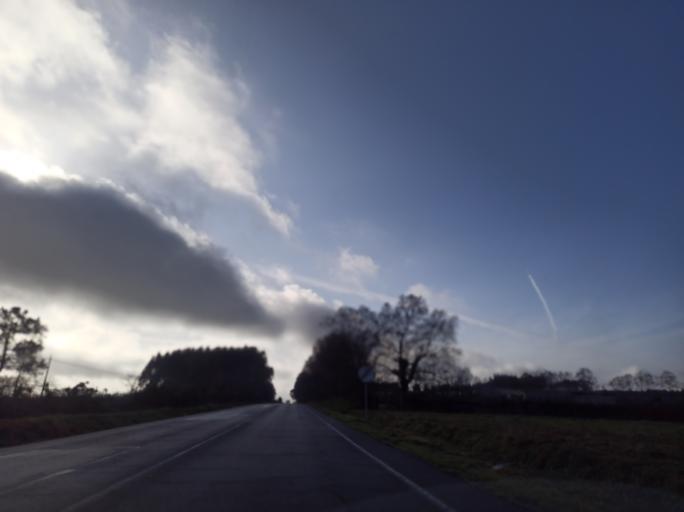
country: ES
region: Galicia
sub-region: Provincia da Coruna
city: Curtis
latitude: 43.1042
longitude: -8.0226
